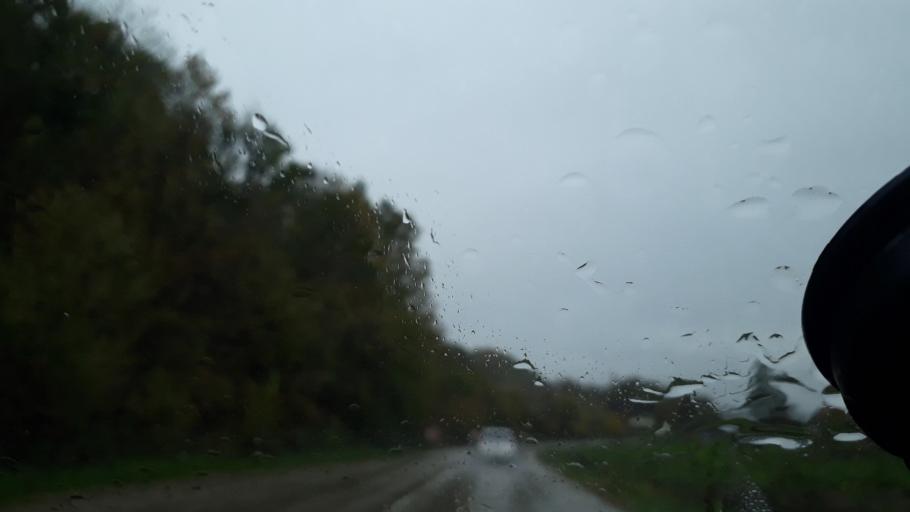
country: BA
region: Republika Srpska
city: Maglajani
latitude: 44.8663
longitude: 17.4135
